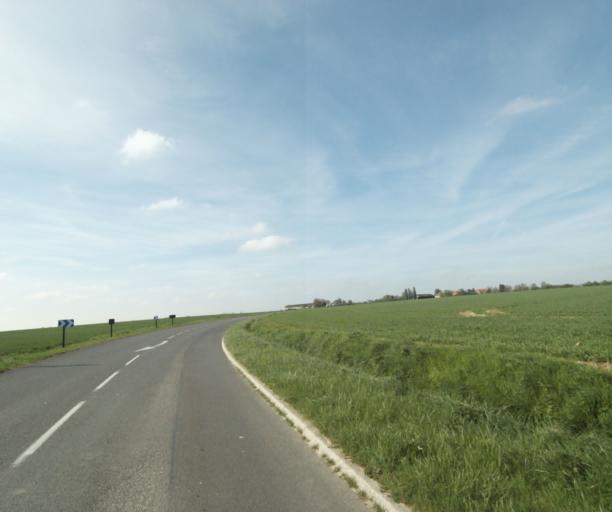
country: FR
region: Ile-de-France
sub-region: Departement de Seine-et-Marne
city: Nangis
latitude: 48.5808
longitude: 3.0460
